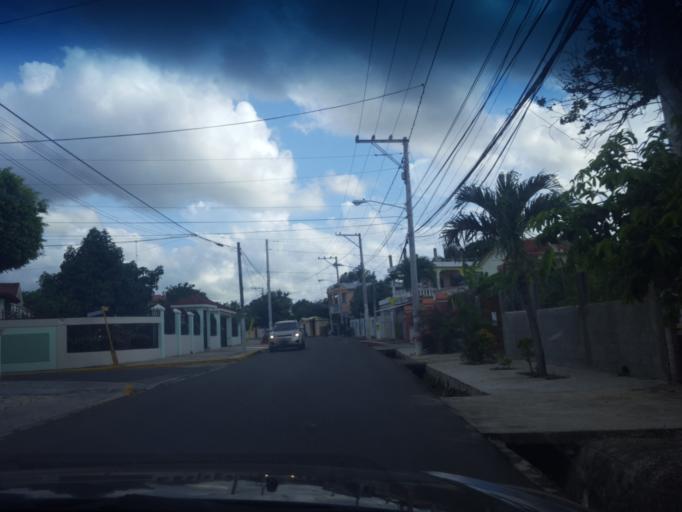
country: DO
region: Santiago
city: Licey al Medio
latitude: 19.3783
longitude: -70.6348
